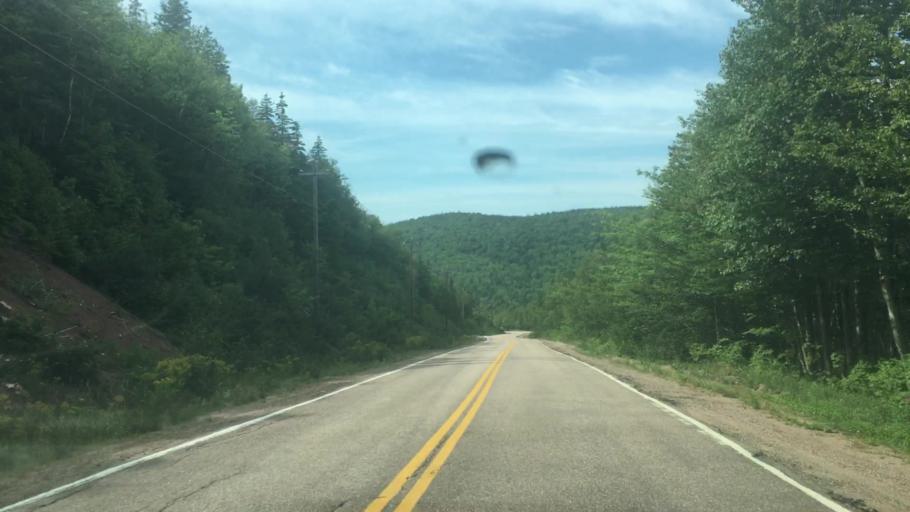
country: CA
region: Nova Scotia
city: Sydney Mines
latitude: 46.6043
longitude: -60.3878
